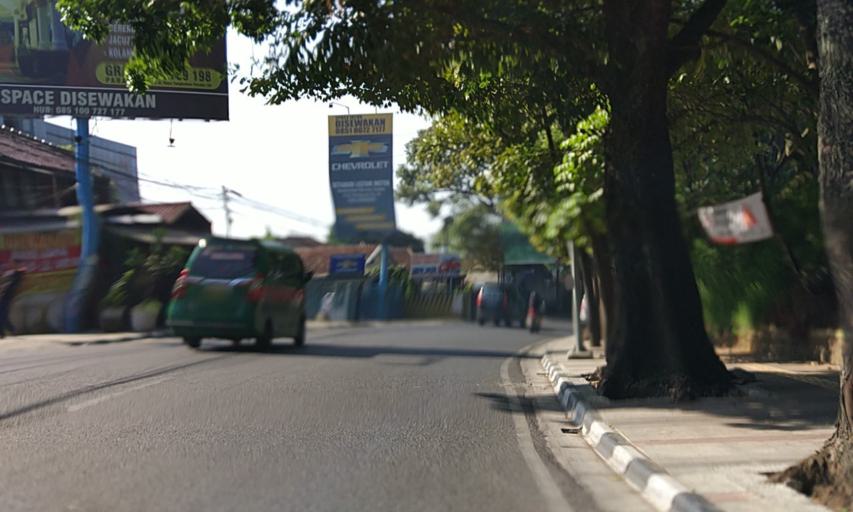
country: ID
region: West Java
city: Bandung
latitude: -6.8833
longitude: 107.6033
